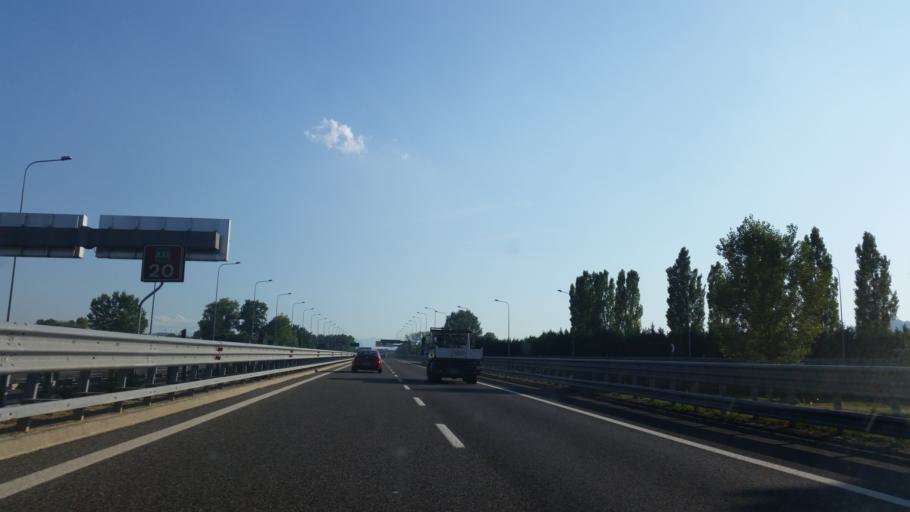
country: IT
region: Piedmont
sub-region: Provincia di Cuneo
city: Govone
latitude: 44.7771
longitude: 8.1096
